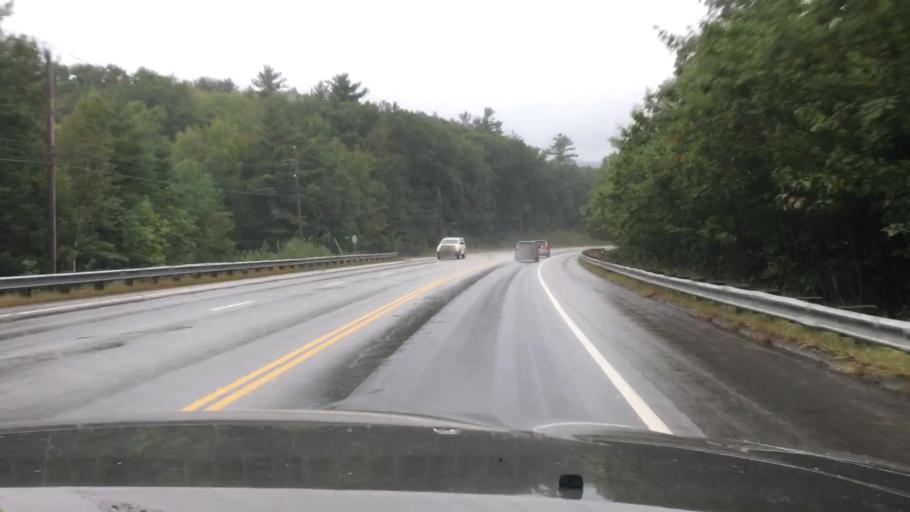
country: US
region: New Hampshire
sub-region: Cheshire County
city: West Swanzey
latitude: 42.9231
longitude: -72.3751
